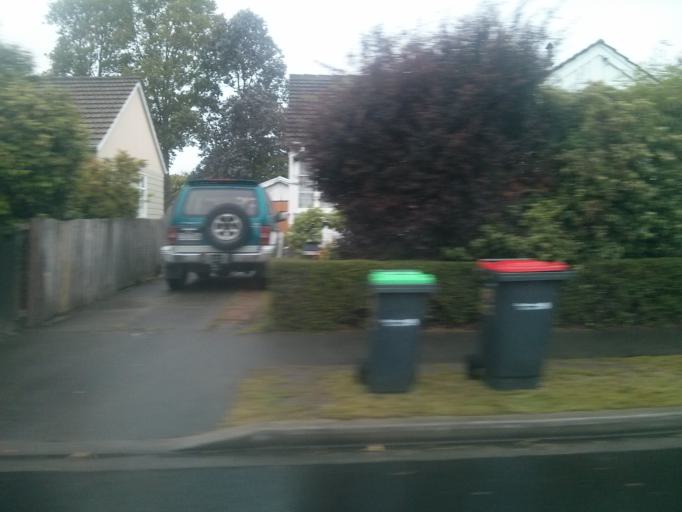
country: NZ
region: Canterbury
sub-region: Christchurch City
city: Christchurch
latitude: -43.5315
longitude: 172.5780
